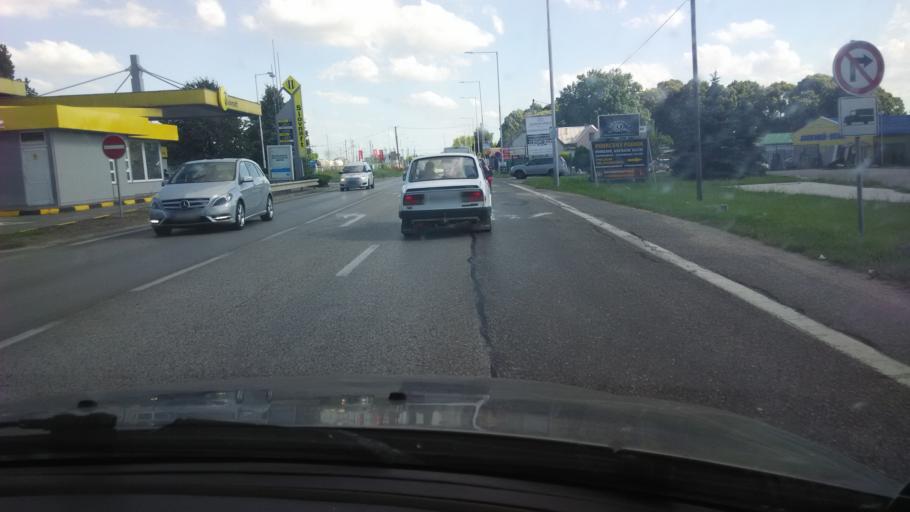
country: SK
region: Nitriansky
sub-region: Okres Nove Zamky
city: Nove Zamky
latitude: 48.0097
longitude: 18.1559
